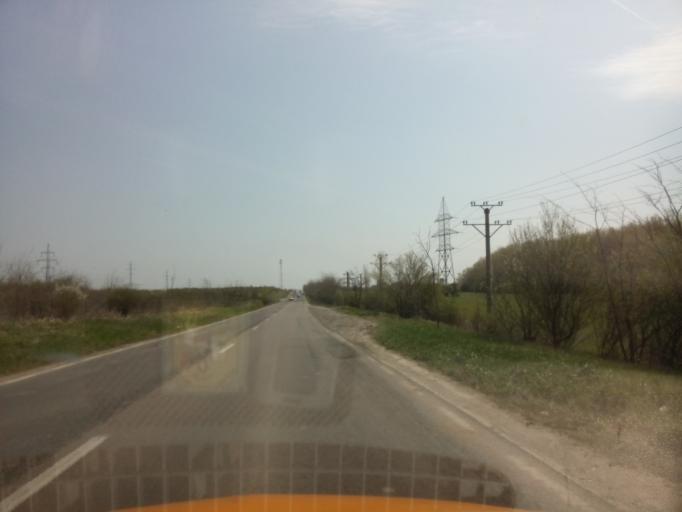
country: RO
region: Calarasi
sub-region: Comuna Budesti
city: Budesti
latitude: 44.2319
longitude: 26.4779
